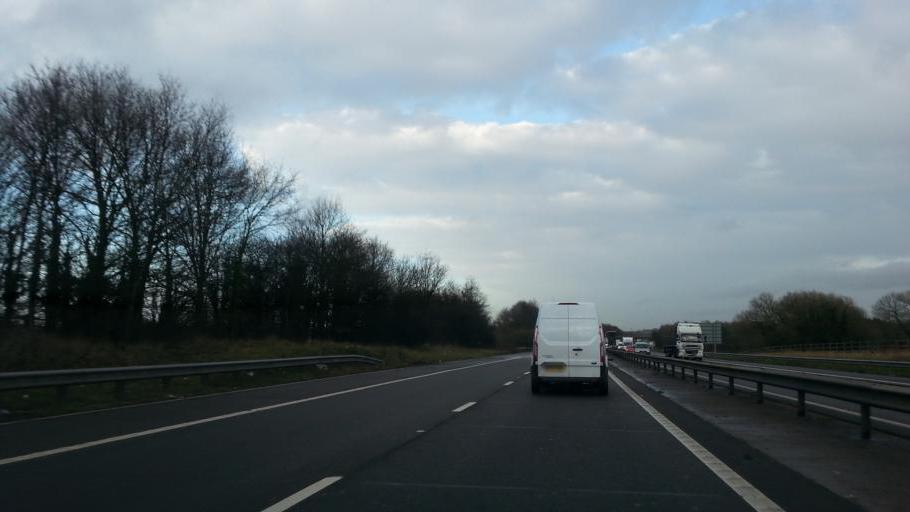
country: GB
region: England
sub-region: Warwickshire
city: Kingsbury
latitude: 52.5583
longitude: -1.7075
